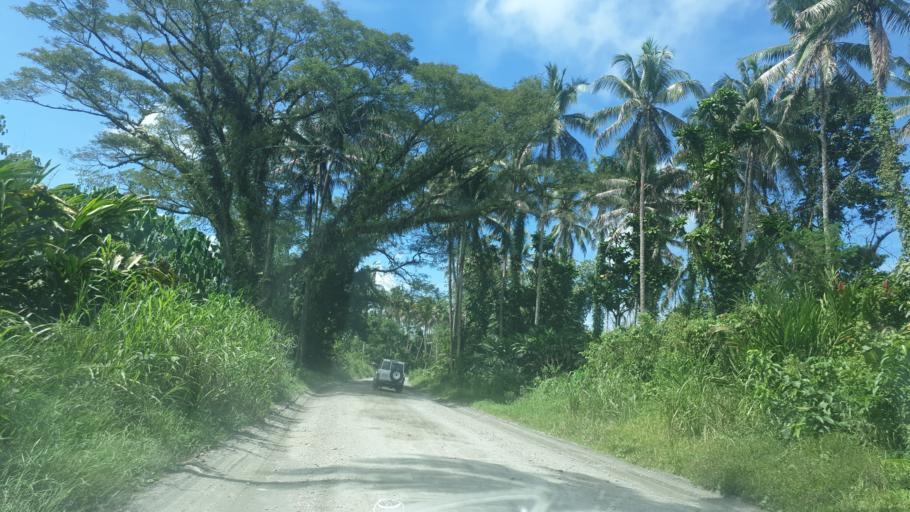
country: PG
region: Bougainville
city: Panguna
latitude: -6.7387
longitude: 155.6720
